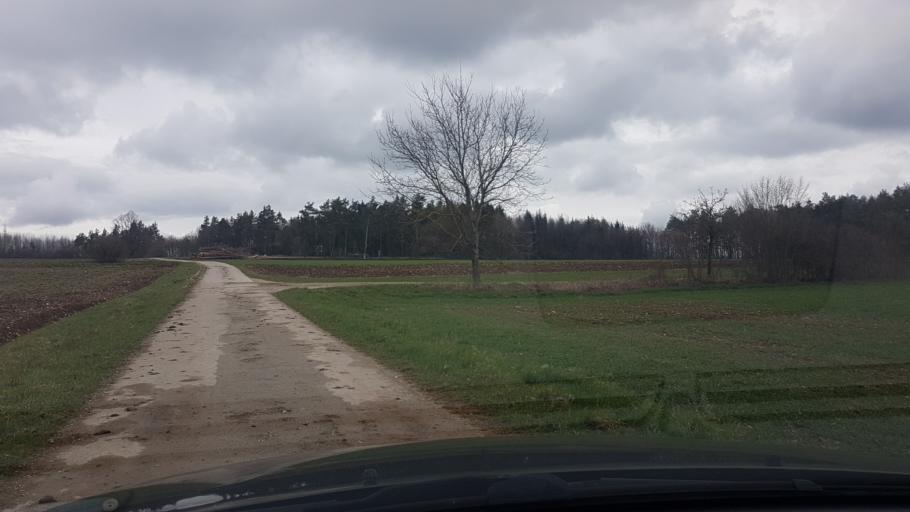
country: DE
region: Bavaria
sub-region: Upper Franconia
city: Heiligenstadt
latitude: 49.8614
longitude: 11.0954
